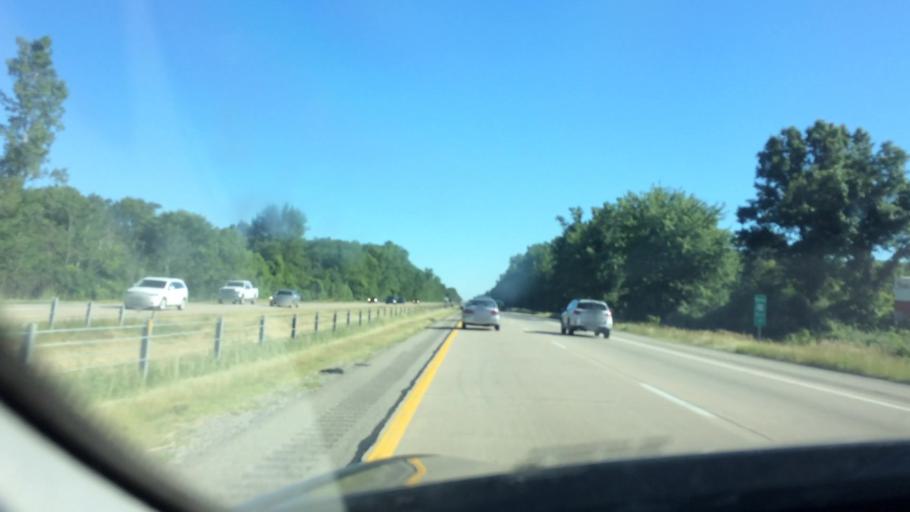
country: US
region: Michigan
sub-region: Monroe County
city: Petersburg
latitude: 41.8779
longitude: -83.6612
